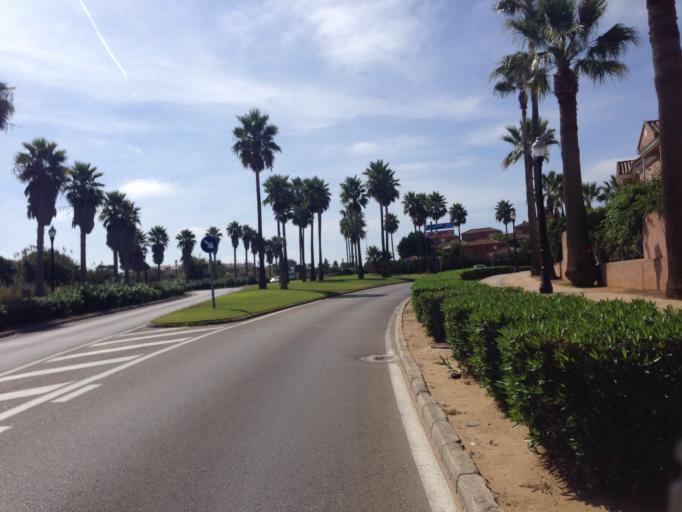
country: ES
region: Andalusia
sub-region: Provincia de Cadiz
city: Chiclana de la Frontera
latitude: 36.3450
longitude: -6.1535
